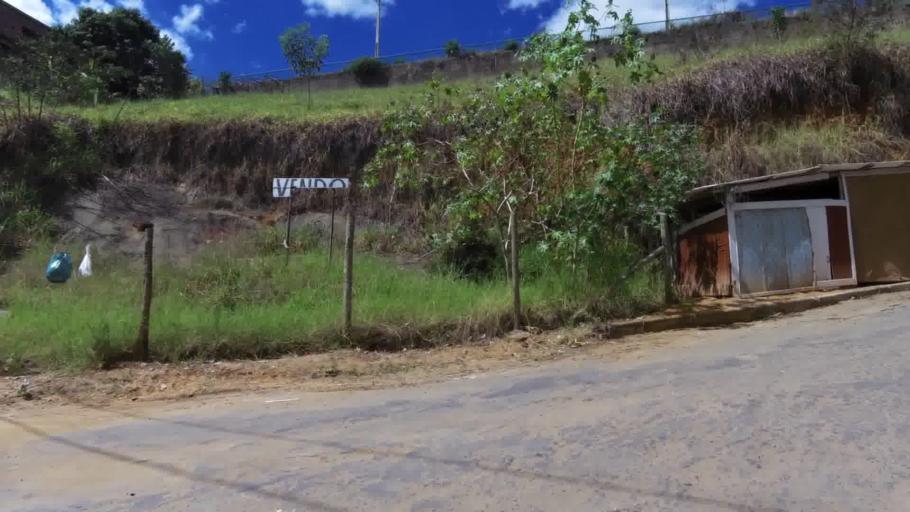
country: BR
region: Espirito Santo
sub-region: Rio Novo Do Sul
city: Rio Novo do Sul
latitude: -20.8683
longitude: -40.9385
